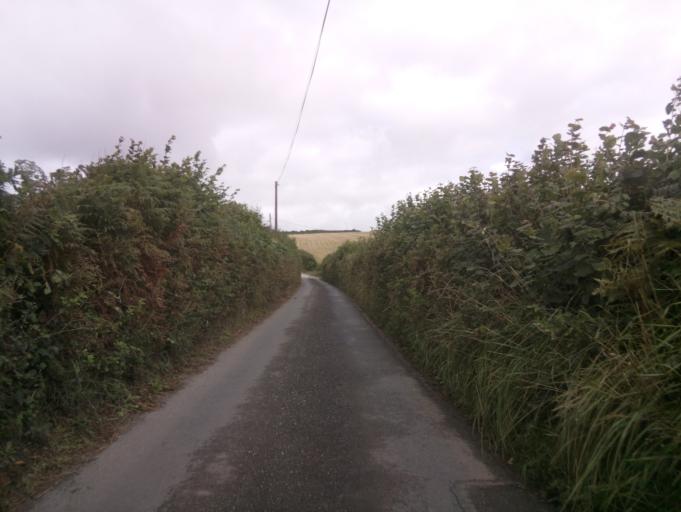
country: GB
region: England
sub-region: Devon
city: Dartmouth
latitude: 50.3345
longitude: -3.5878
